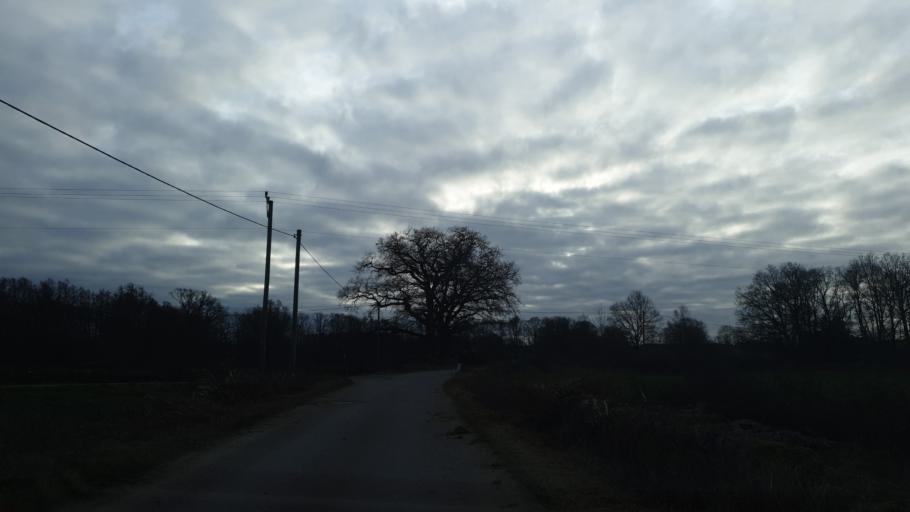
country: SE
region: Kalmar
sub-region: Torsas Kommun
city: Torsas
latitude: 56.3250
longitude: 16.0405
